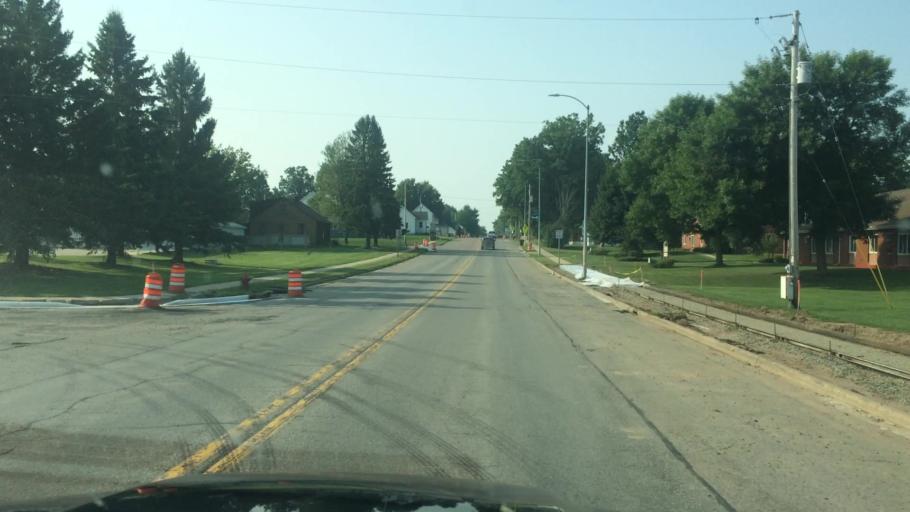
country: US
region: Wisconsin
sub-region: Marathon County
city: Stratford
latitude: 44.8074
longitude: -90.0793
